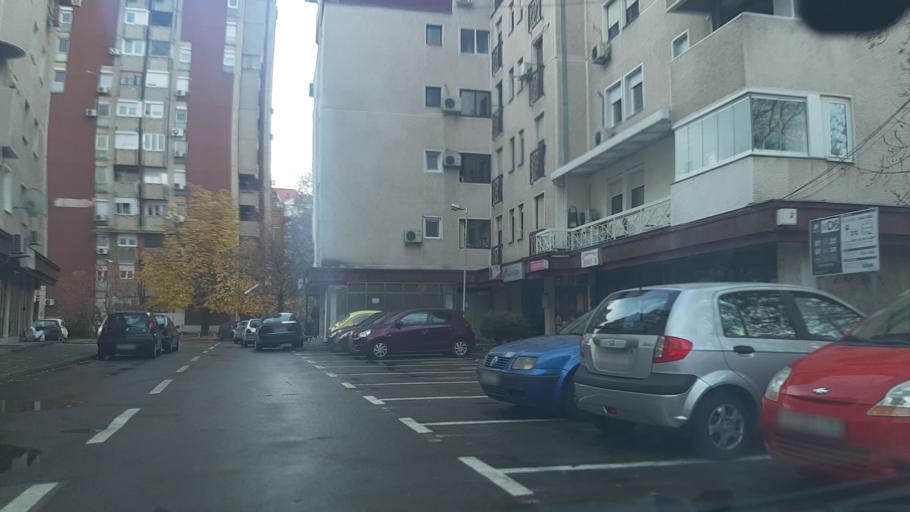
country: MK
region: Karpos
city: Skopje
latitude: 41.9891
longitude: 21.4529
